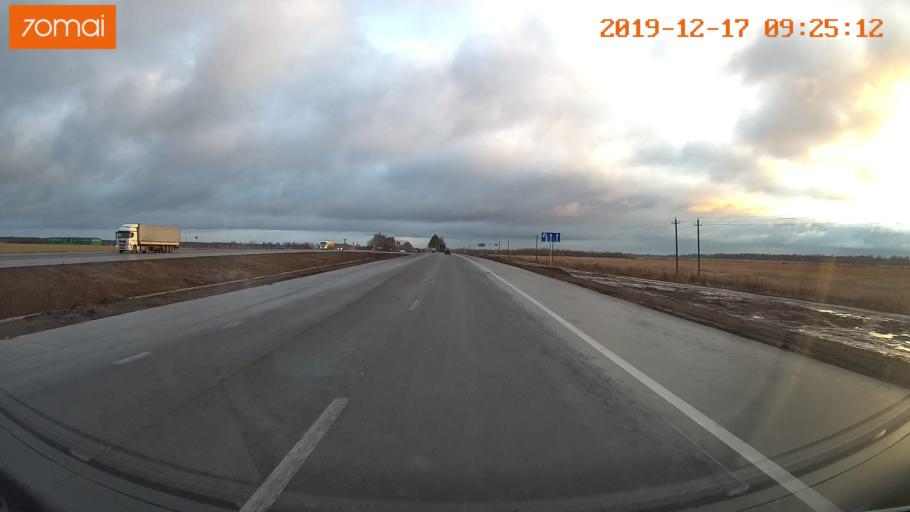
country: RU
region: Vladimir
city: Vorsha
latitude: 56.0404
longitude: 40.0506
